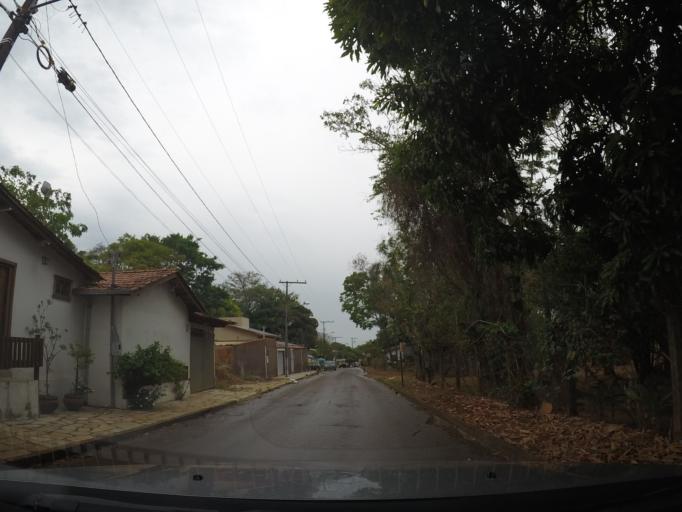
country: BR
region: Goias
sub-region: Pirenopolis
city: Pirenopolis
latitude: -15.8494
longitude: -48.9510
